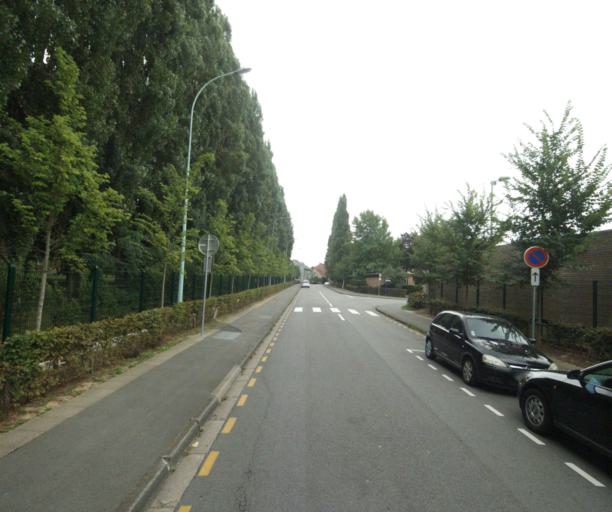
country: FR
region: Nord-Pas-de-Calais
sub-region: Departement du Nord
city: Mons-en-Baroeul
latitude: 50.6443
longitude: 3.1266
